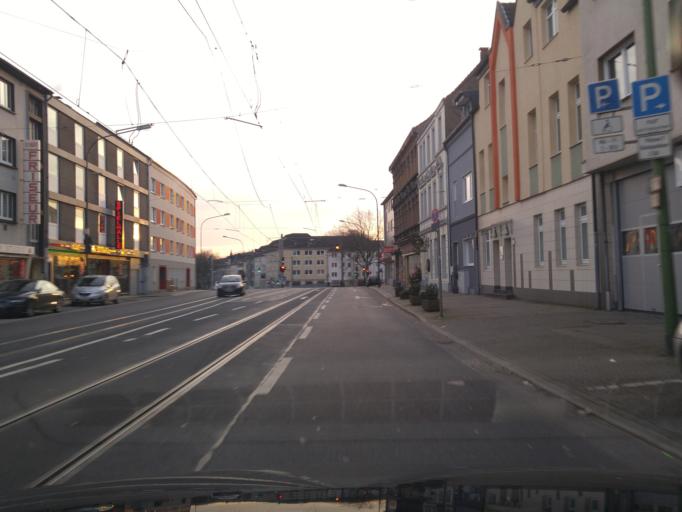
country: DE
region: North Rhine-Westphalia
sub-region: Regierungsbezirk Dusseldorf
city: Essen
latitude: 51.4489
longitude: 7.0357
